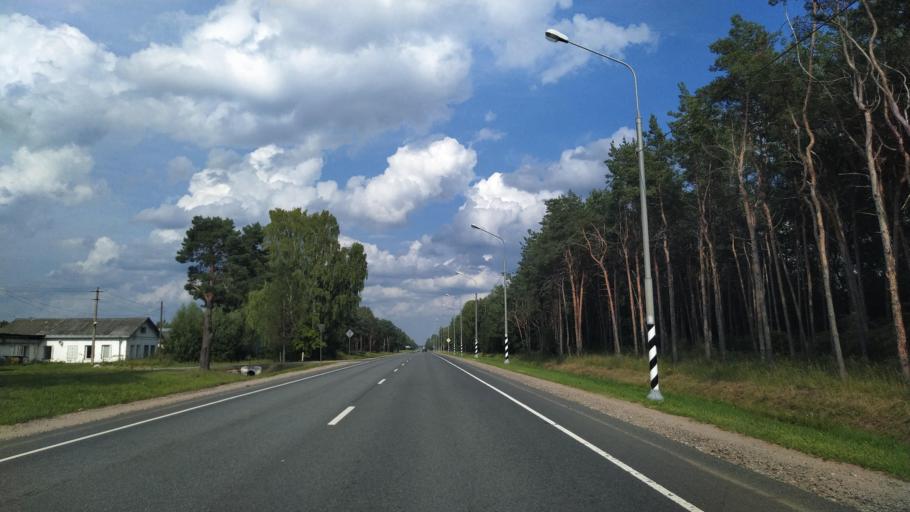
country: RU
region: Novgorod
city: Shimsk
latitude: 58.1797
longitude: 30.5359
